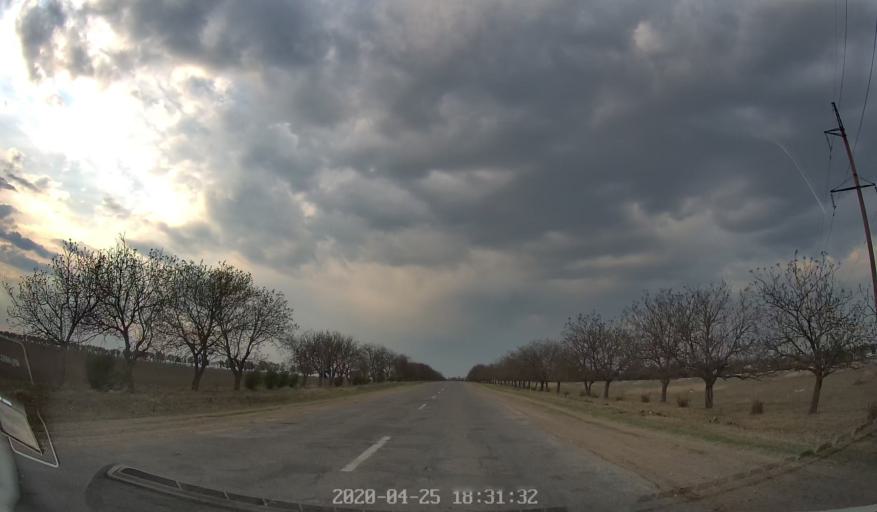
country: MD
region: Criuleni
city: Criuleni
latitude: 47.2186
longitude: 29.1468
